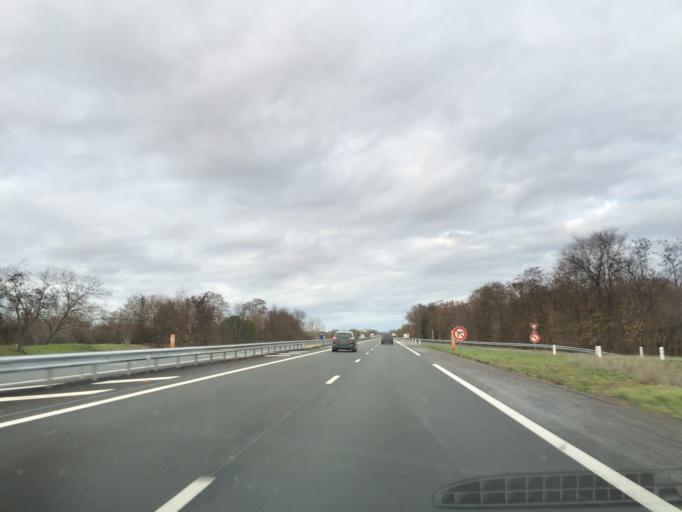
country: FR
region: Poitou-Charentes
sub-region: Departement des Deux-Sevres
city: Fors
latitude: 46.2225
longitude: -0.4483
